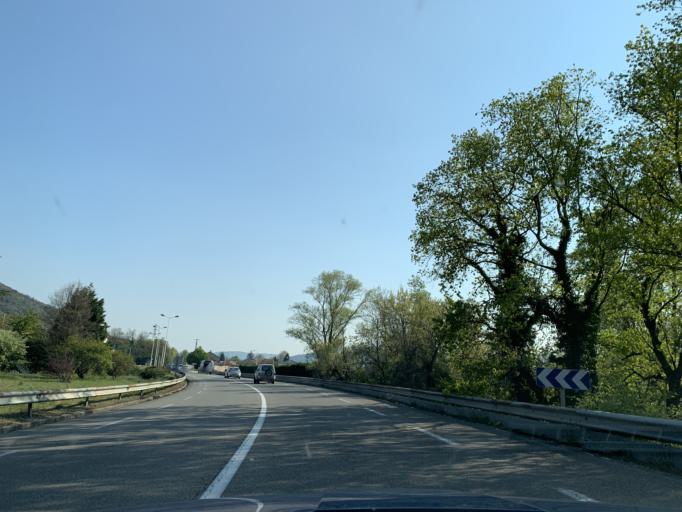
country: FR
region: Rhone-Alpes
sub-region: Departement de la Drome
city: Saint-Vallier
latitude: 45.1387
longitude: 4.8166
